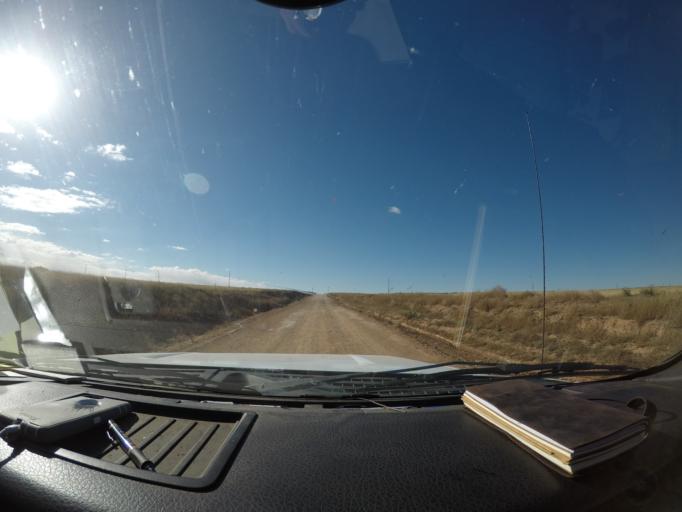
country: US
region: New Mexico
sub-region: Curry County
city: Clovis
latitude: 34.5797
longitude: -103.1333
